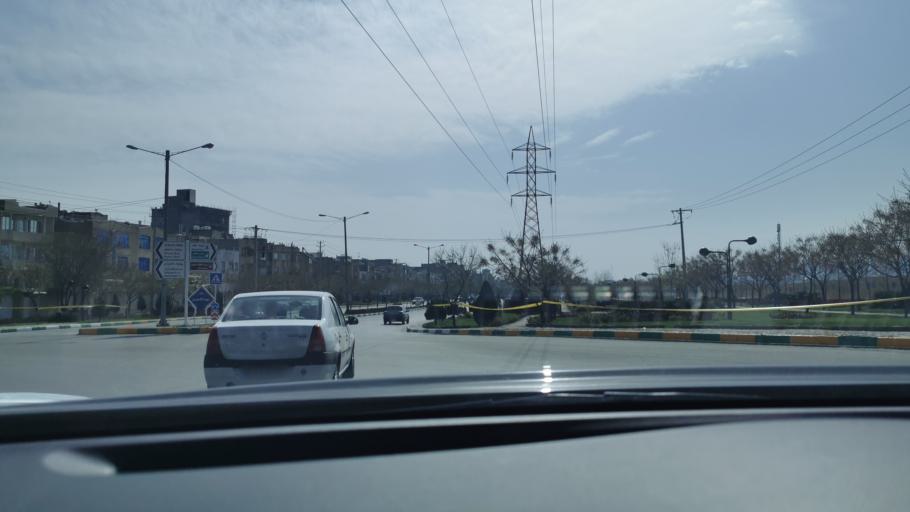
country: IR
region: Razavi Khorasan
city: Mashhad
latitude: 36.2880
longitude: 59.5344
